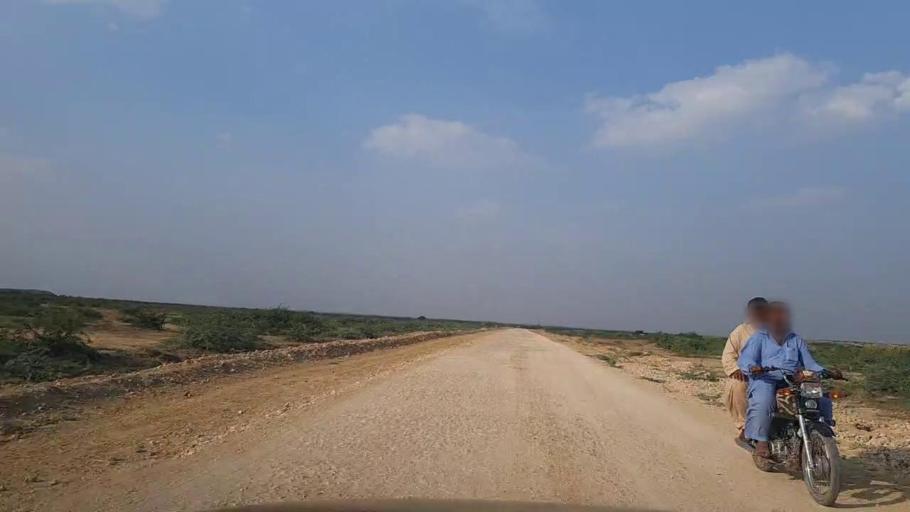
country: PK
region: Sindh
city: Gharo
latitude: 24.8121
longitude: 67.7419
